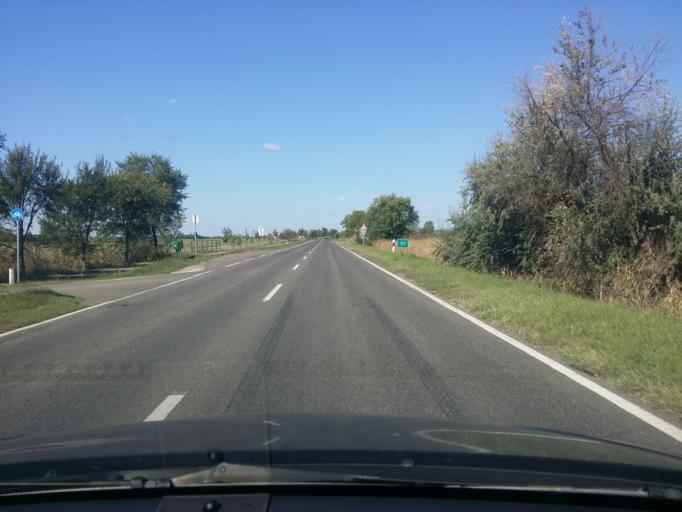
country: HU
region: Bacs-Kiskun
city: Kiskunfelegyhaza
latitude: 46.6715
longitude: 19.8569
